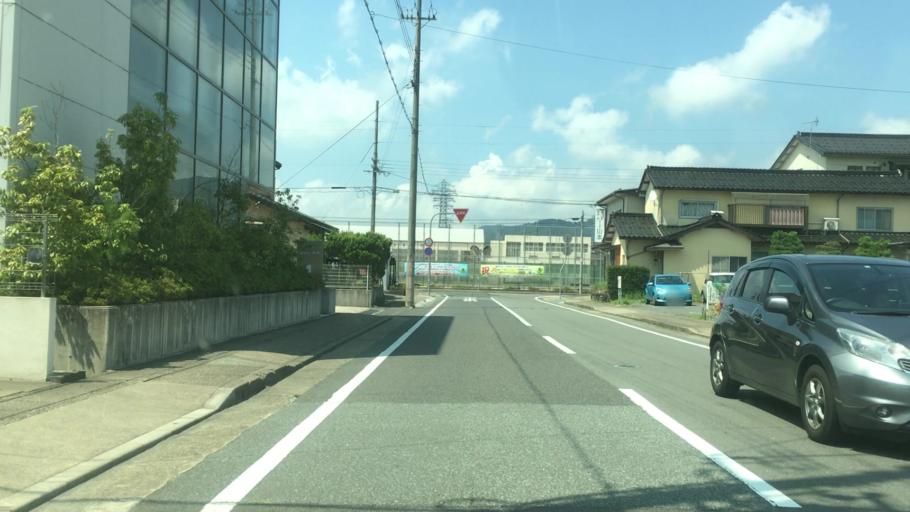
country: JP
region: Hyogo
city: Toyooka
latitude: 35.5484
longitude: 134.8196
